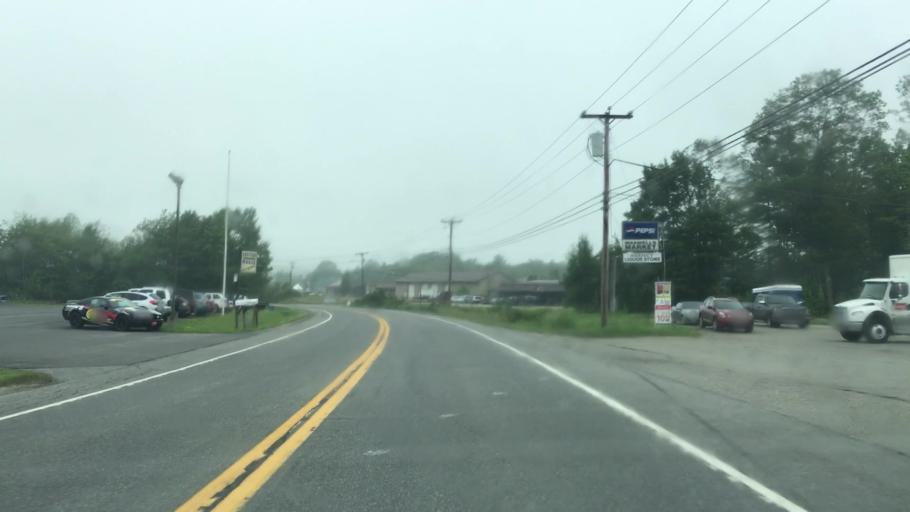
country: US
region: Maine
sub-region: Lincoln County
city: Wiscasset
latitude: 44.0370
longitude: -69.6727
